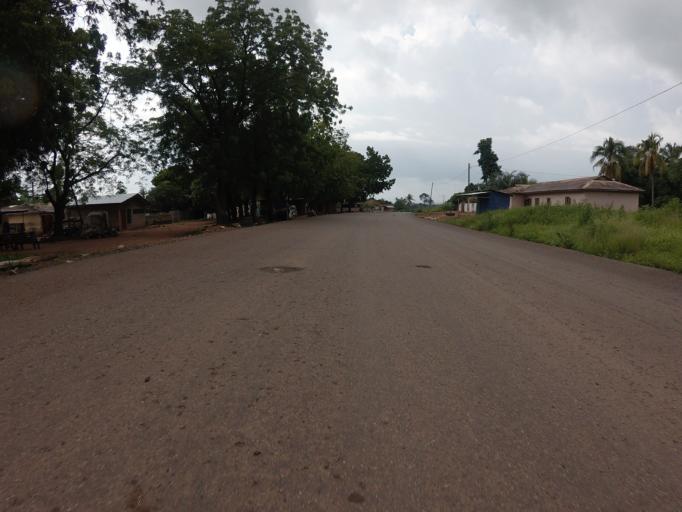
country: GH
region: Volta
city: Kpandu
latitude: 6.9516
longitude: 0.4583
